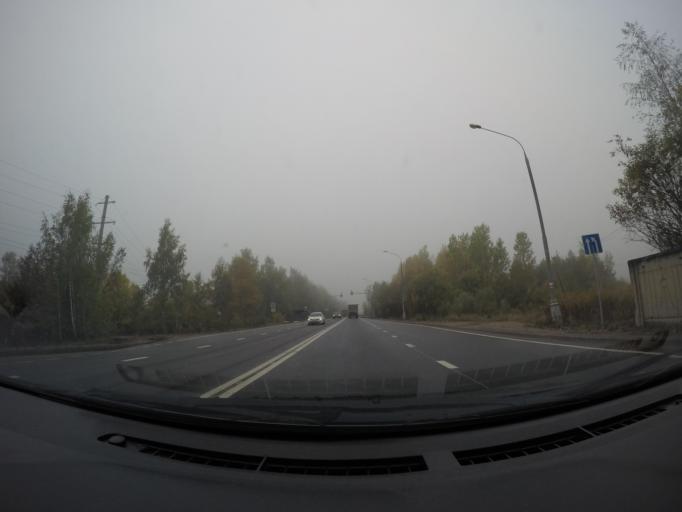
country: RU
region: Moskovskaya
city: Rumyantsevo
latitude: 55.8749
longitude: 36.5556
